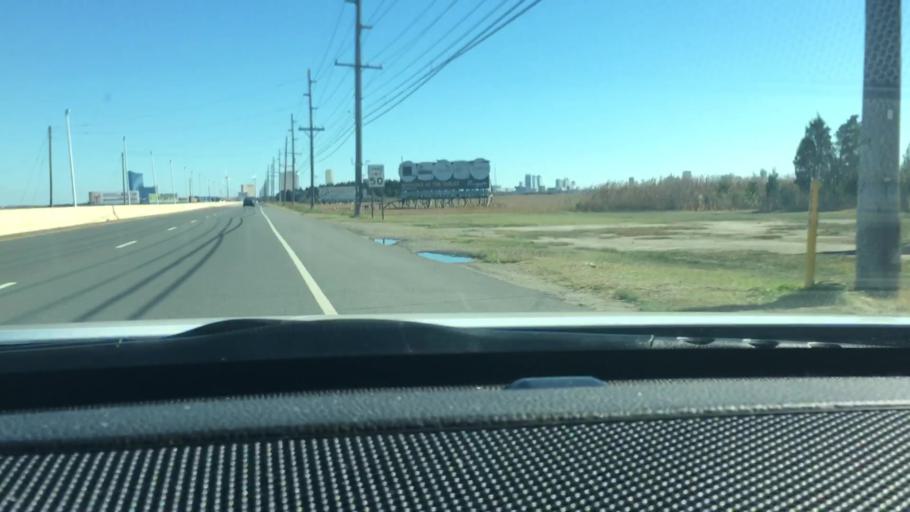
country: US
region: New Jersey
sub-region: Atlantic County
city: Pleasantville
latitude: 39.3894
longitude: -74.4835
